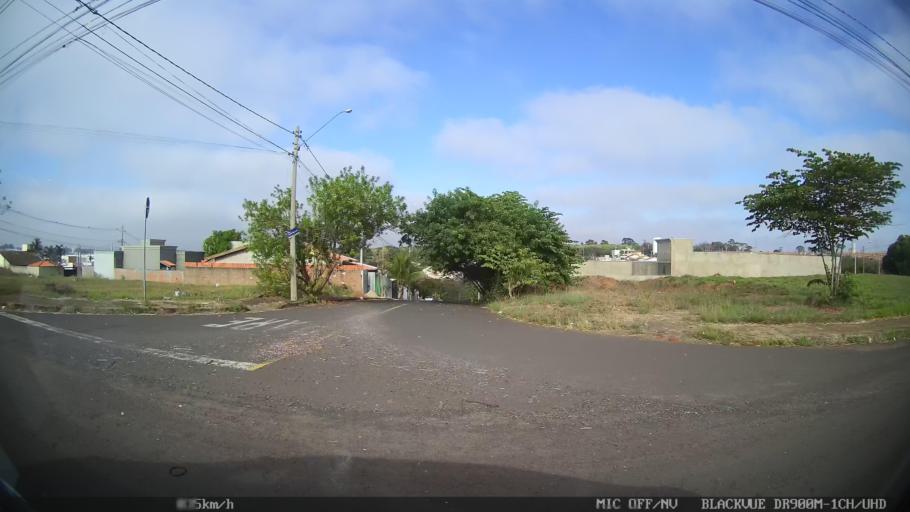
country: BR
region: Sao Paulo
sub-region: Sao Jose Do Rio Preto
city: Sao Jose do Rio Preto
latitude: -20.8011
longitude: -49.4314
